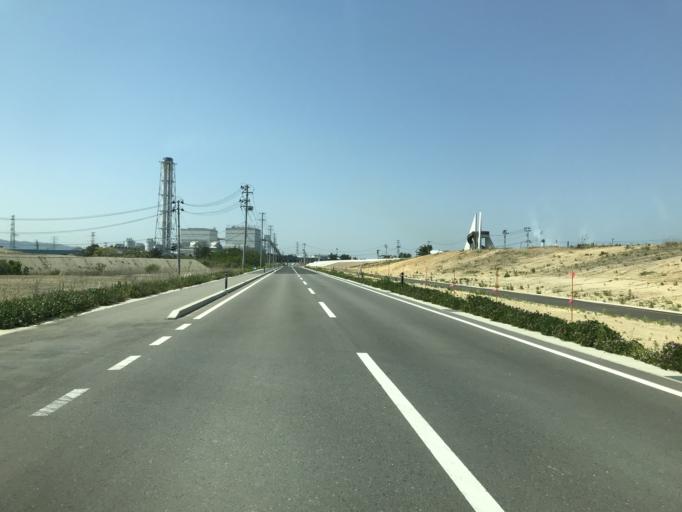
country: JP
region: Miyagi
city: Marumori
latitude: 37.8333
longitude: 140.9540
